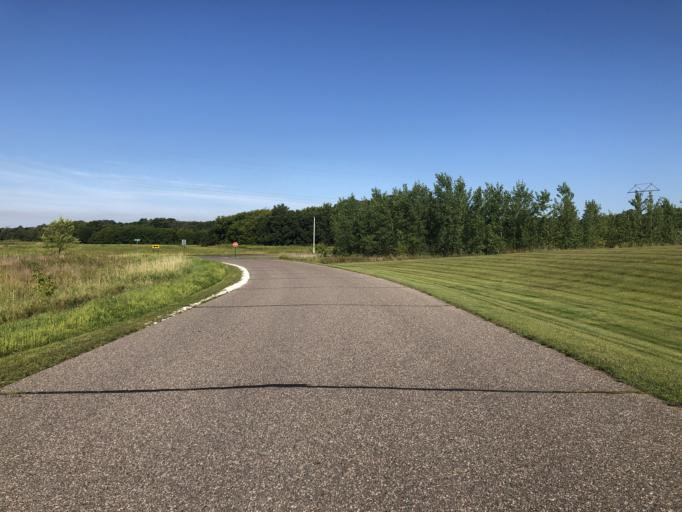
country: US
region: Minnesota
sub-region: Sherburne County
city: Becker
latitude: 45.4241
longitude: -93.8388
